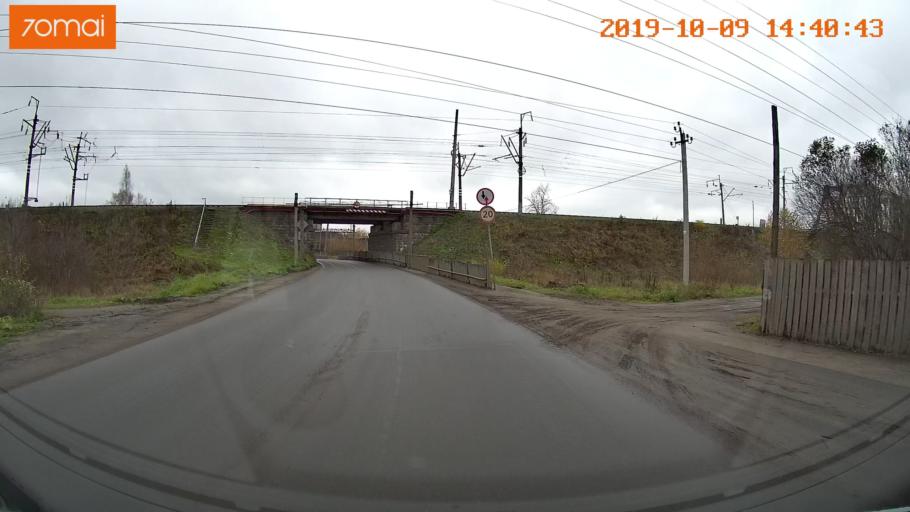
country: RU
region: Kostroma
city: Buy
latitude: 58.4748
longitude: 41.5292
